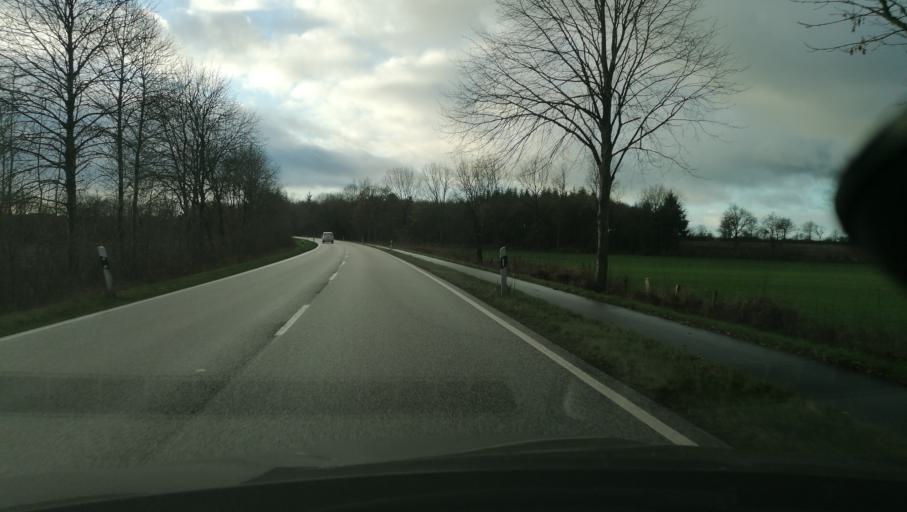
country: DE
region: Schleswig-Holstein
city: Sarzbuttel
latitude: 54.1112
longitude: 9.2070
